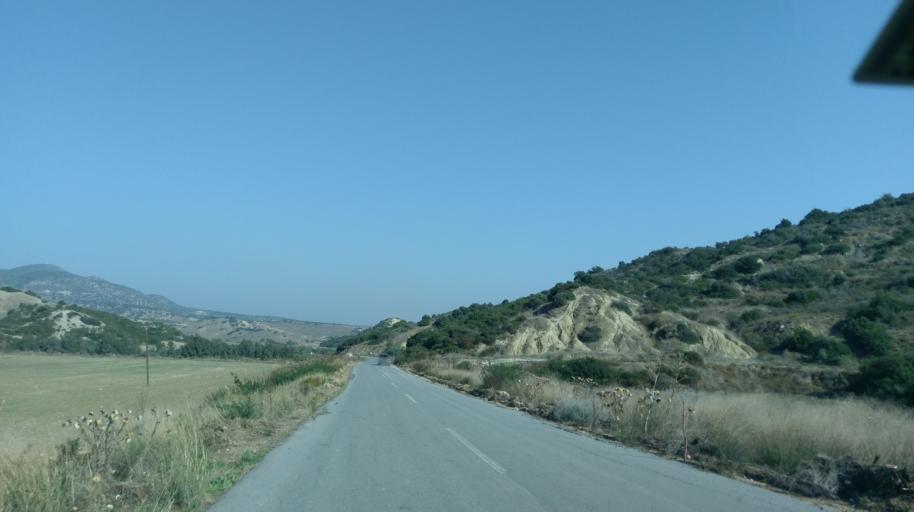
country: CY
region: Ammochostos
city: Leonarisso
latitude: 35.4985
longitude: 34.2282
